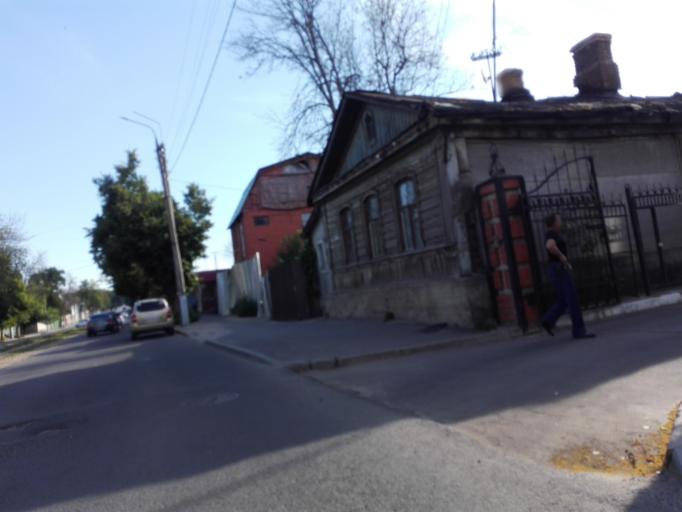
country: RU
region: Orjol
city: Orel
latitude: 52.9543
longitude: 36.0566
